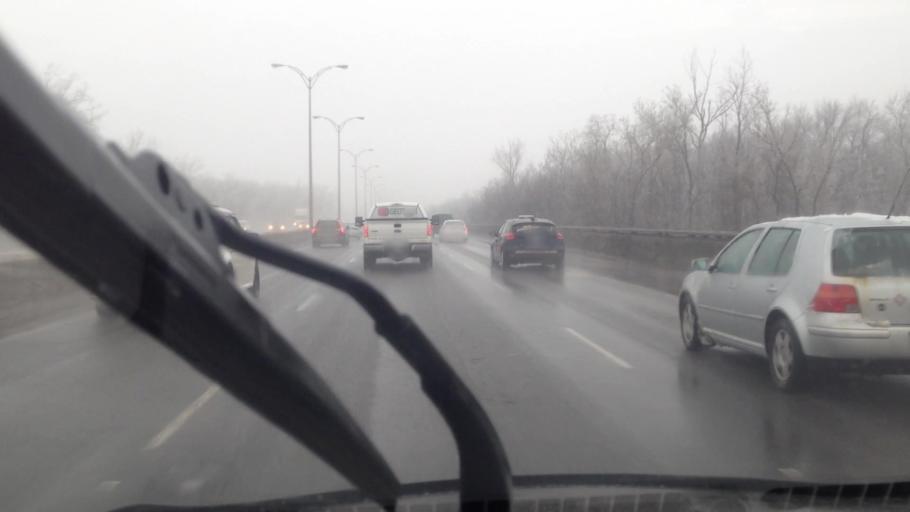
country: CA
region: Quebec
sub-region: Laurentides
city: Boisbriand
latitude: 45.6101
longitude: -73.8126
